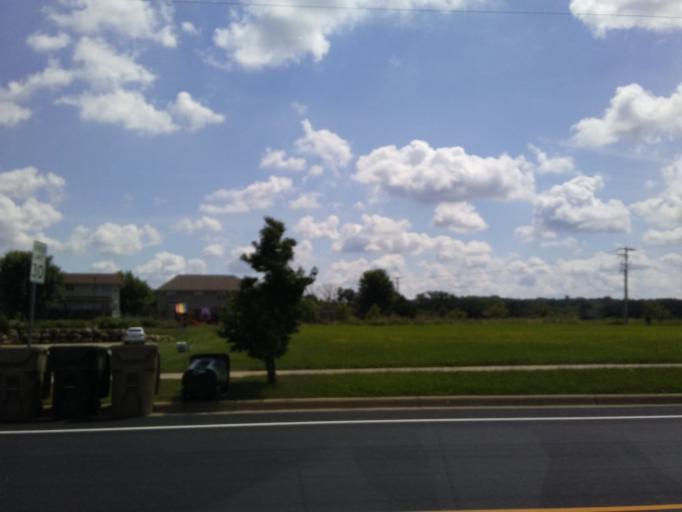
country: US
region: Wisconsin
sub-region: Dane County
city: Verona
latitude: 43.0020
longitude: -89.4992
